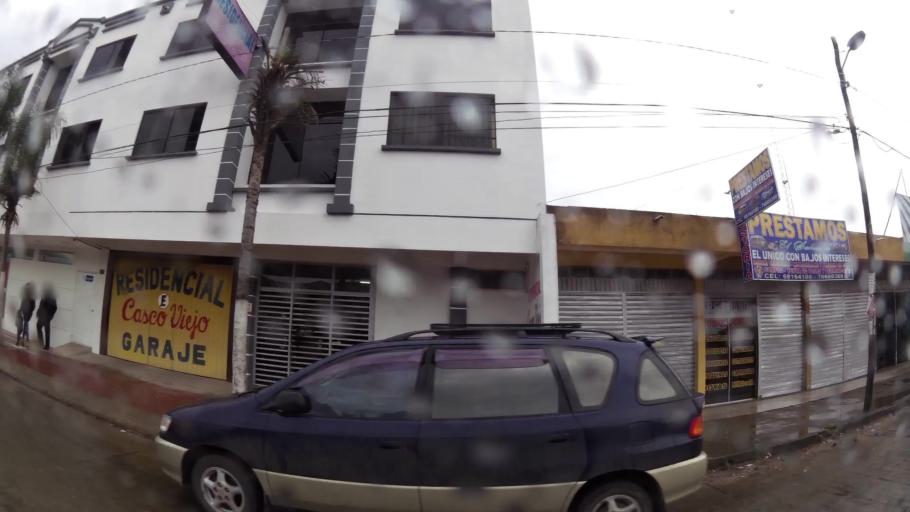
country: BO
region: Santa Cruz
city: Santa Cruz de la Sierra
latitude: -17.8023
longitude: -63.1353
